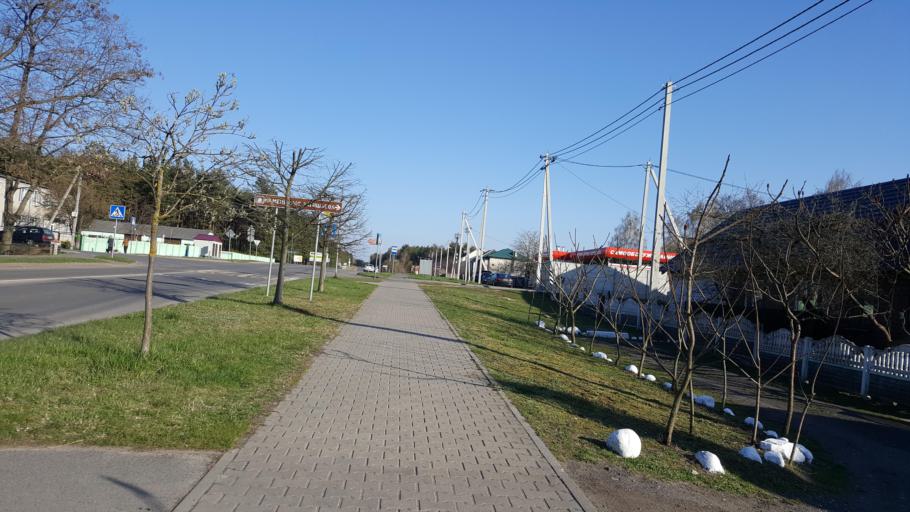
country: BY
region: Brest
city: Kamyanyets
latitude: 52.3942
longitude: 23.8321
